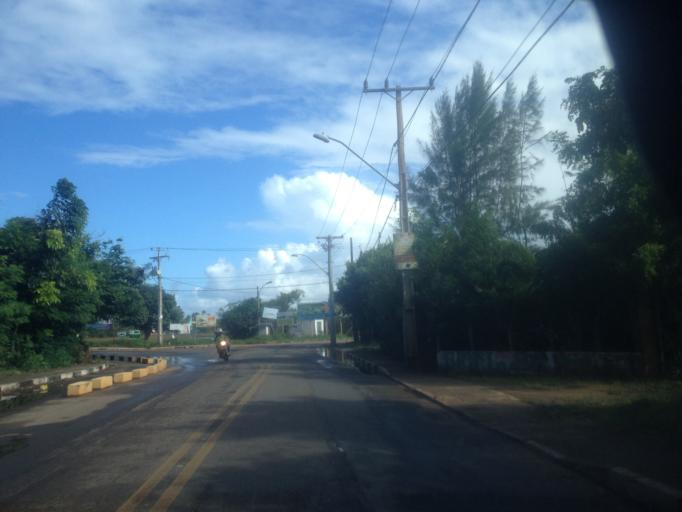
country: BR
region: Bahia
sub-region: Mata De Sao Joao
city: Mata de Sao Joao
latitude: -12.6043
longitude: -38.0409
